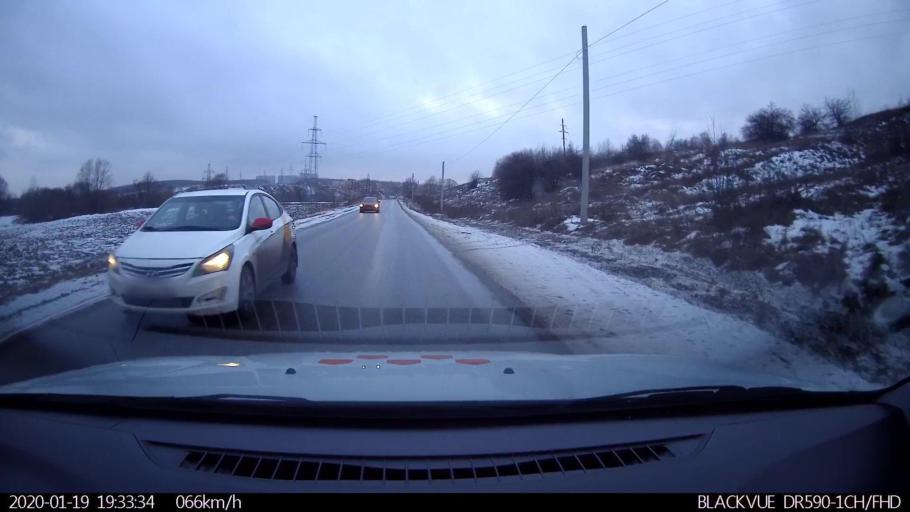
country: RU
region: Nizjnij Novgorod
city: Afonino
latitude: 56.2410
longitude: 44.0933
